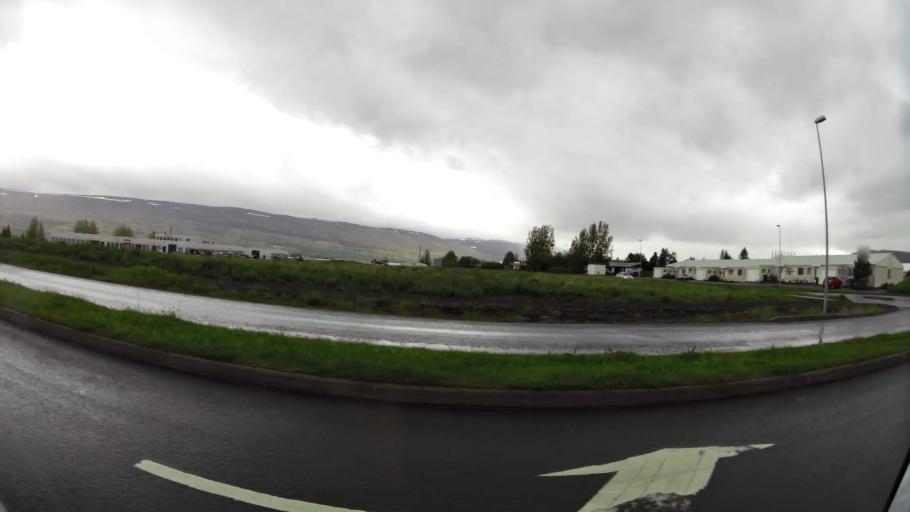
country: IS
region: Northeast
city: Akureyri
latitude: 65.6984
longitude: -18.1432
